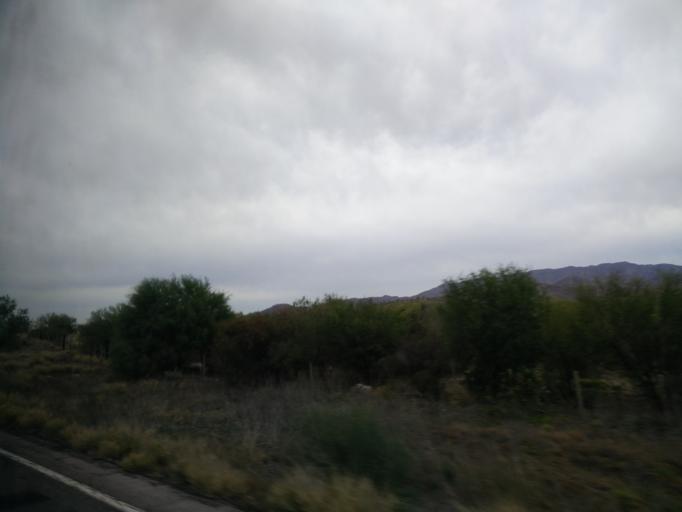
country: MX
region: Sonora
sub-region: Hermosillo
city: Miguel Aleman (La Doce)
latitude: 28.5269
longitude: -111.0469
